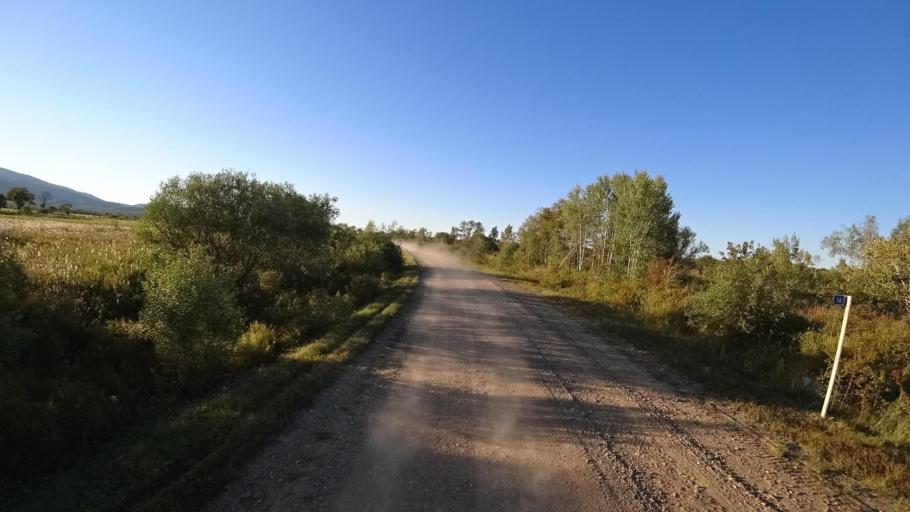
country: RU
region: Primorskiy
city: Kirovskiy
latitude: 44.8124
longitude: 133.6161
